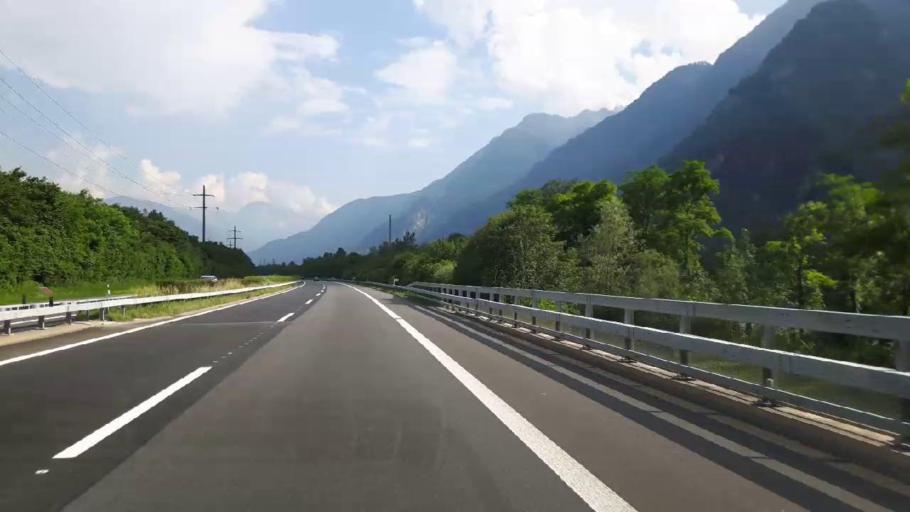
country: CH
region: Ticino
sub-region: Riviera District
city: Lodrino
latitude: 46.3099
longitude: 8.9824
